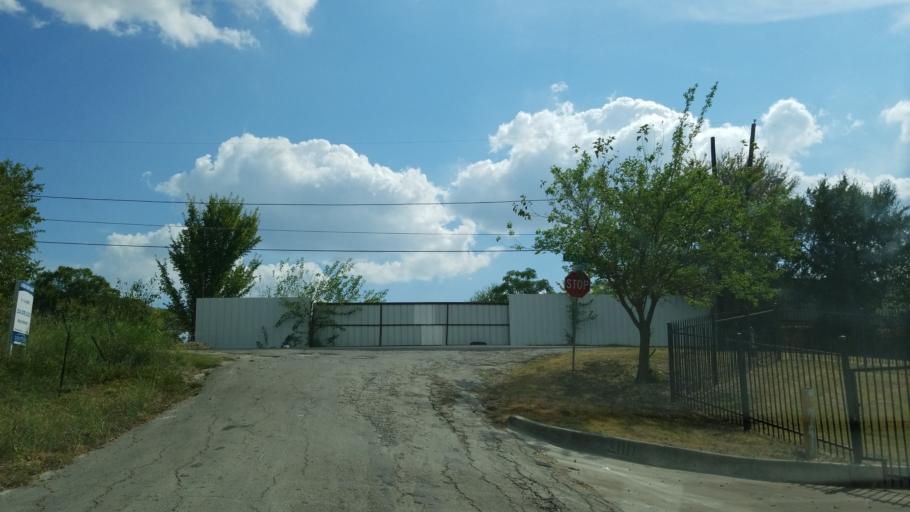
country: US
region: Texas
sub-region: Dallas County
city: Dallas
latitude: 32.7716
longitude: -96.8472
